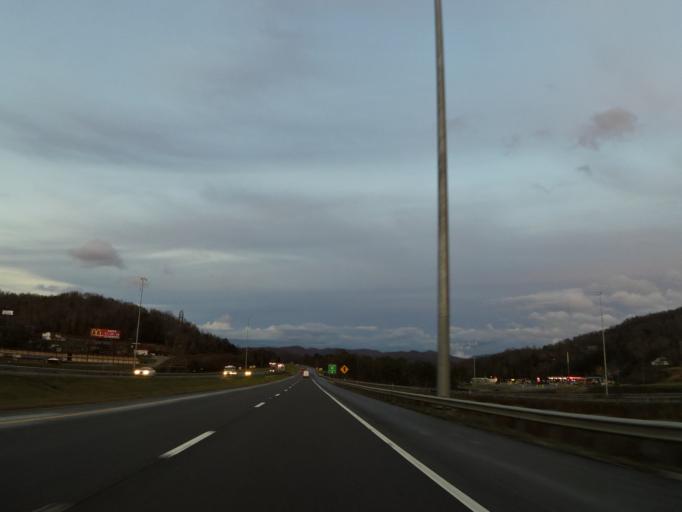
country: US
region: Tennessee
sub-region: Campbell County
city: Jellico
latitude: 36.5771
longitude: -84.1134
